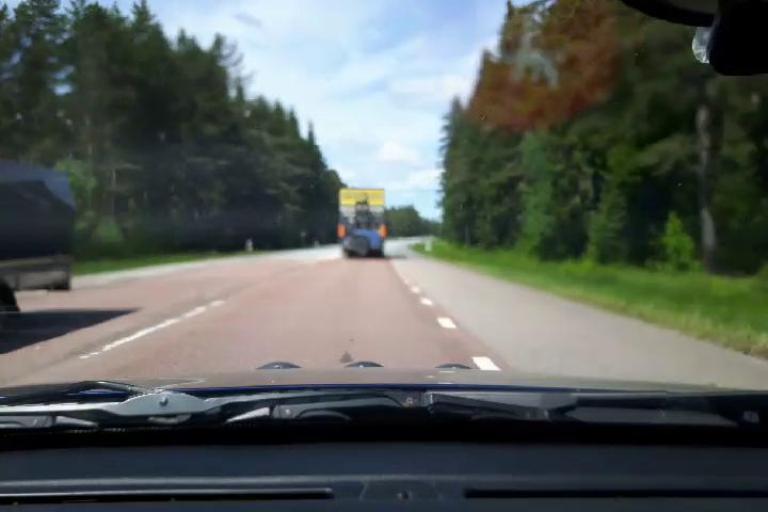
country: SE
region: Uppsala
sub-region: Tierps Kommun
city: Tierp
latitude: 60.1821
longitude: 17.4793
